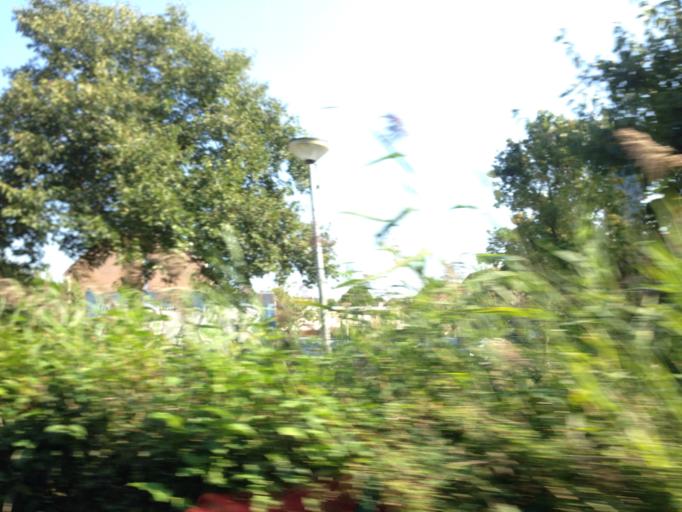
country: NL
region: Flevoland
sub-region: Gemeente Almere
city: Almere Stad
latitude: 52.3652
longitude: 5.2088
